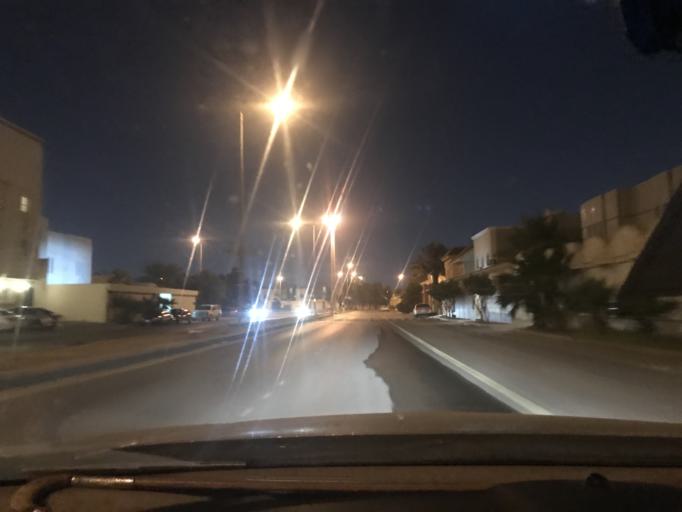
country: SA
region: Ar Riyad
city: Riyadh
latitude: 24.7591
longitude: 46.7445
